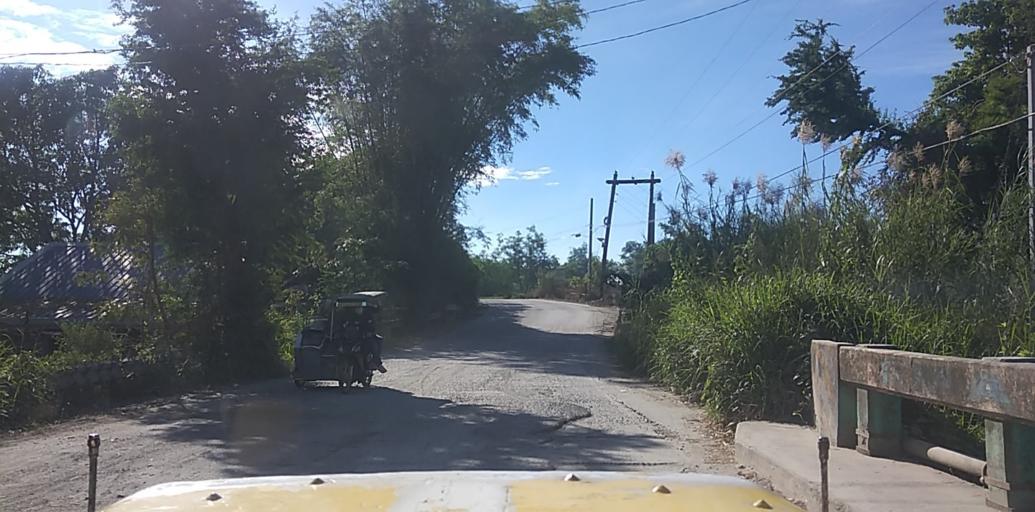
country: PH
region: Central Luzon
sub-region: Province of Pampanga
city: Anao
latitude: 15.1213
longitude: 120.7011
